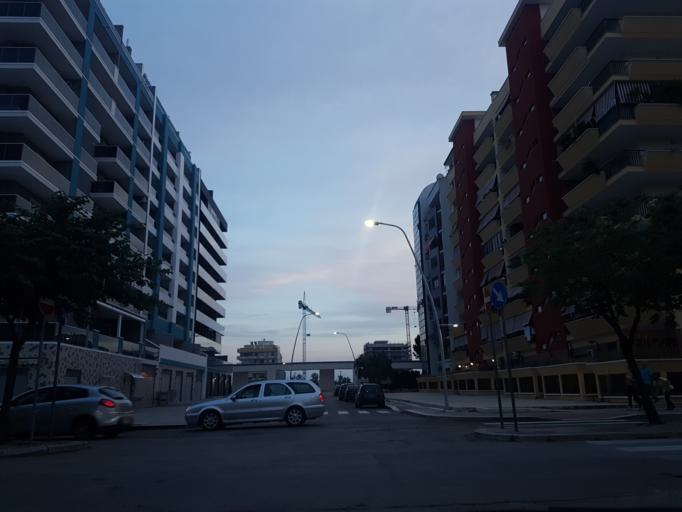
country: IT
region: Apulia
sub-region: Provincia di Barletta - Andria - Trani
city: Barletta
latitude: 41.3062
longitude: 16.2747
